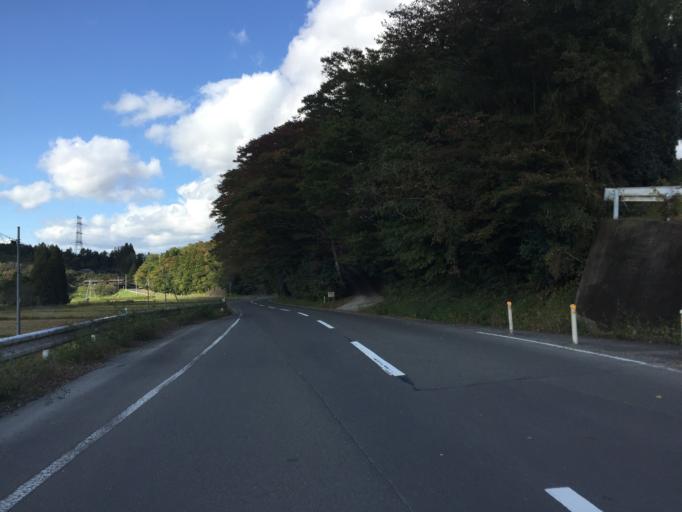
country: JP
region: Miyagi
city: Marumori
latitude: 37.8513
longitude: 140.8322
